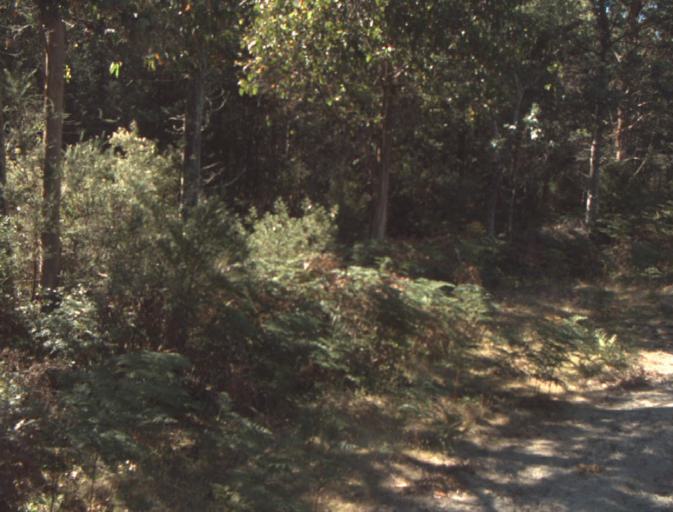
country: AU
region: Tasmania
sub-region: Dorset
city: Scottsdale
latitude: -41.2694
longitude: 147.3762
